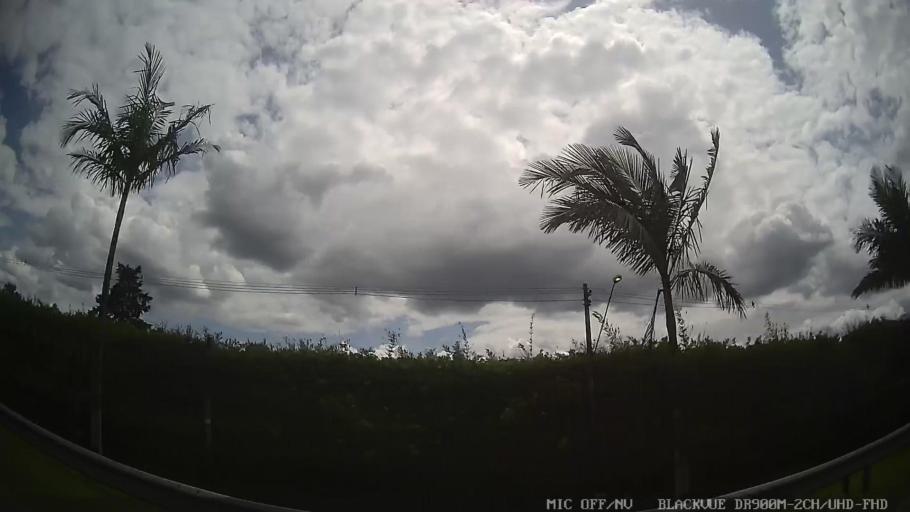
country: BR
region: Sao Paulo
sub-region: Suzano
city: Suzano
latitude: -23.5911
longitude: -46.2557
